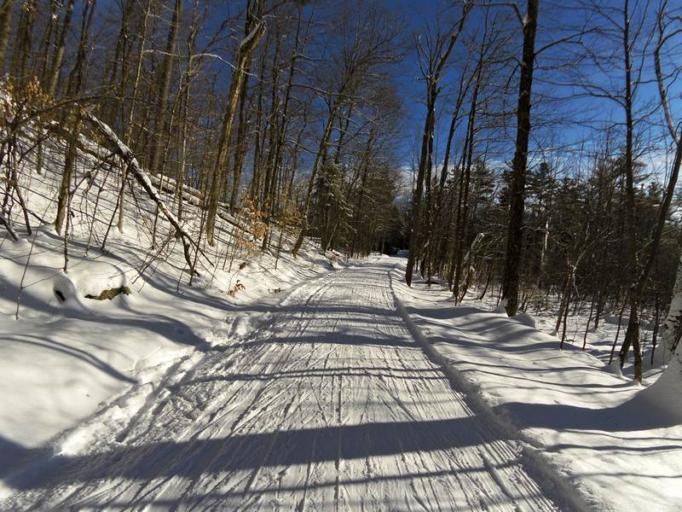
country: CA
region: Quebec
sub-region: Outaouais
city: Wakefield
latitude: 45.5074
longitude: -75.8871
